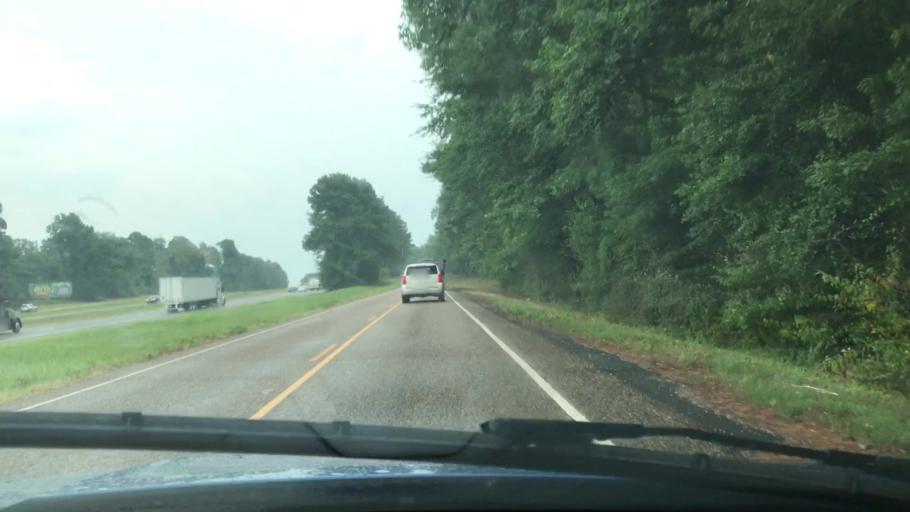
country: US
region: Texas
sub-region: Harrison County
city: Waskom
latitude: 32.4849
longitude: -94.1215
